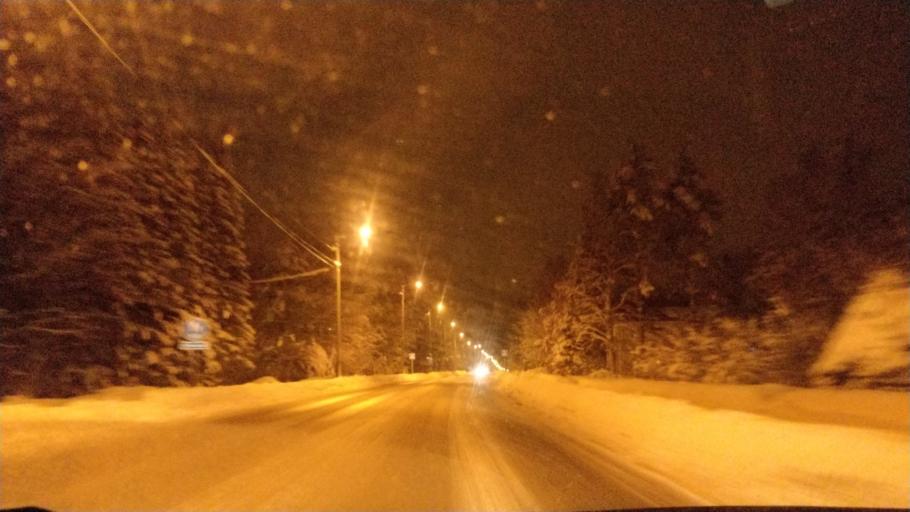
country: FI
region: Lapland
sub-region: Rovaniemi
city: Rovaniemi
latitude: 66.3736
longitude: 25.3824
